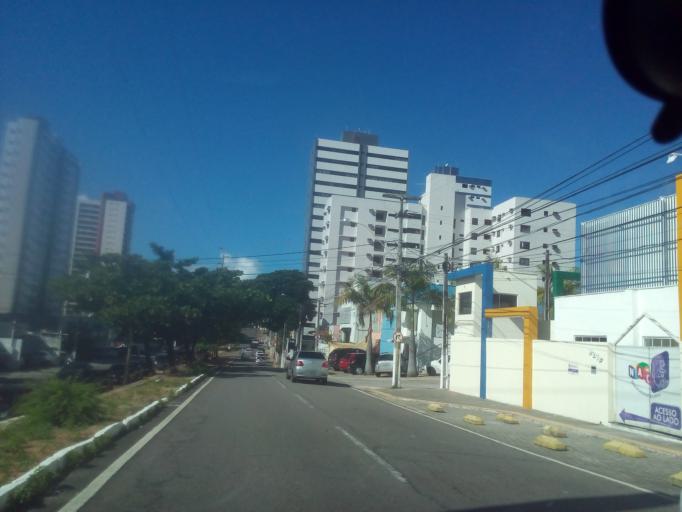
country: BR
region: Rio Grande do Norte
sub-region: Natal
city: Natal
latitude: -5.8038
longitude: -35.2052
